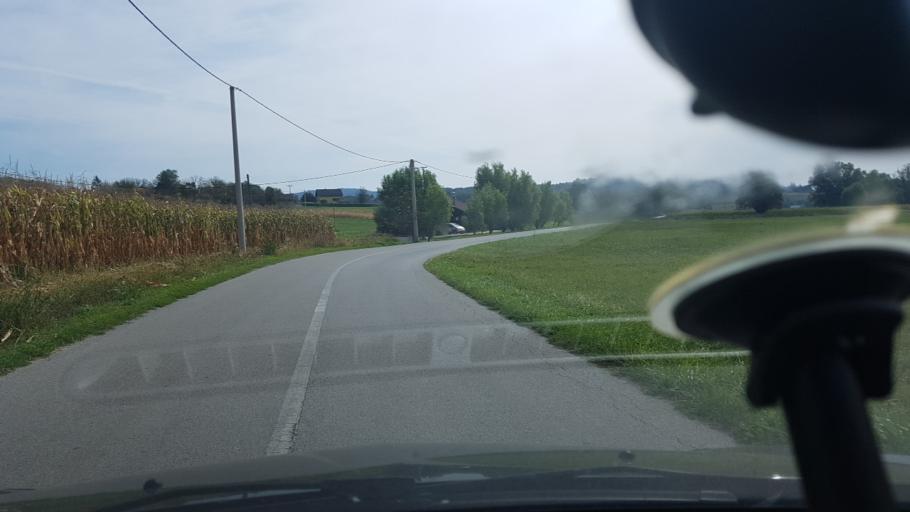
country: HR
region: Varazdinska
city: Remetinec
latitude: 46.1081
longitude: 16.2538
